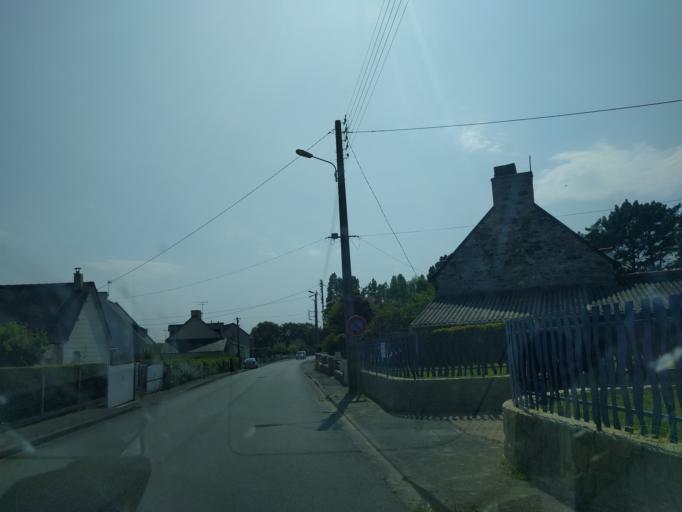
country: FR
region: Brittany
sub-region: Departement des Cotes-d'Armor
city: Erquy
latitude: 48.6379
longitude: -2.4330
